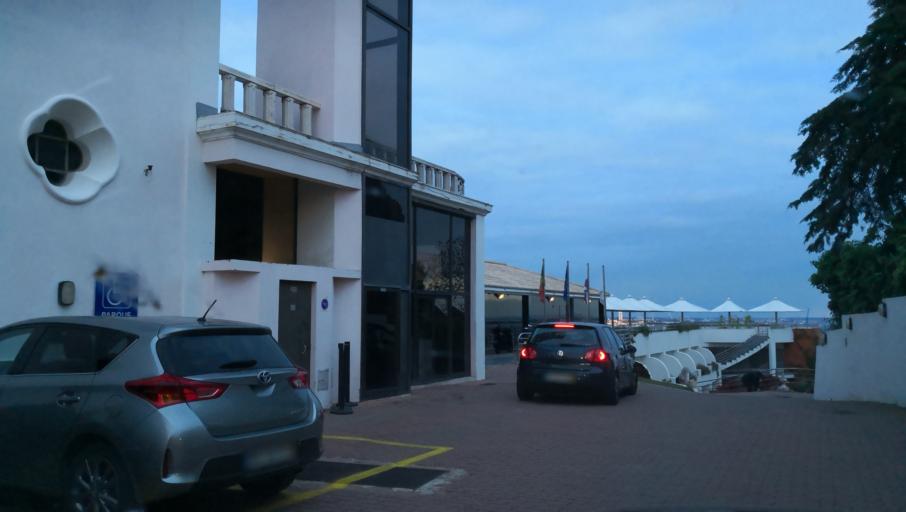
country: PT
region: Setubal
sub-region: Setubal
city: Setubal
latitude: 38.5308
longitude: -8.9023
